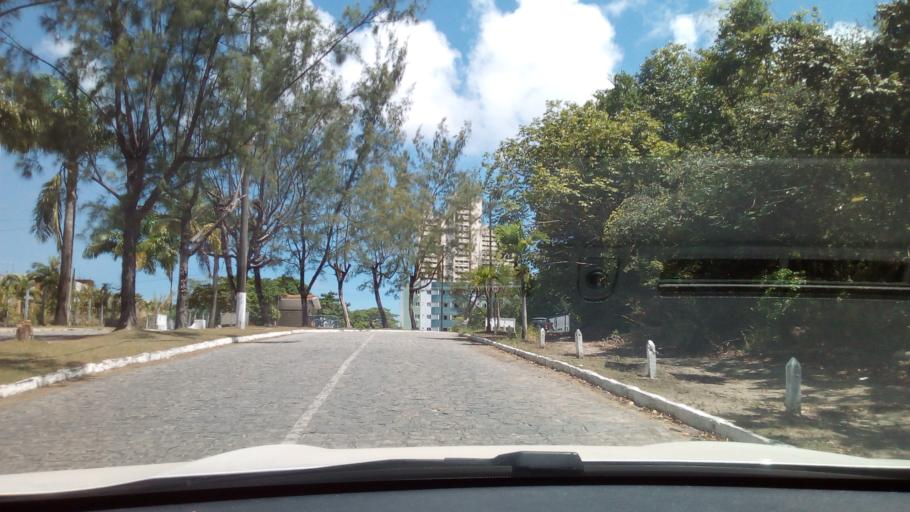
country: BR
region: Paraiba
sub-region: Joao Pessoa
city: Joao Pessoa
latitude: -7.1573
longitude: -34.8526
